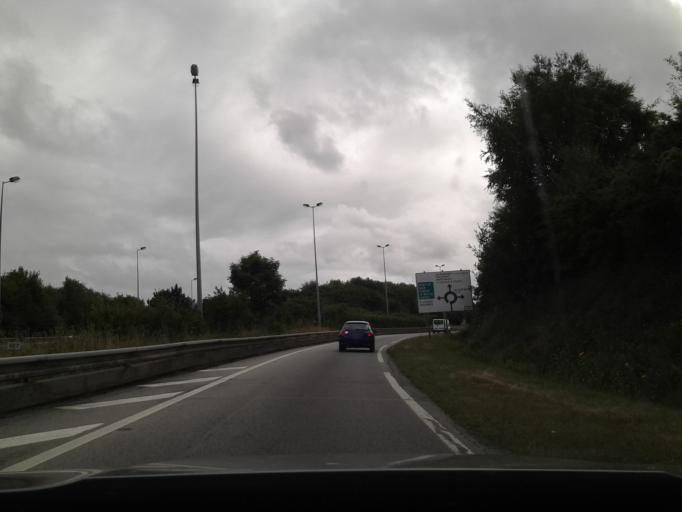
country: FR
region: Lower Normandy
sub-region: Departement de la Manche
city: La Glacerie
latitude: 49.6015
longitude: -1.5945
